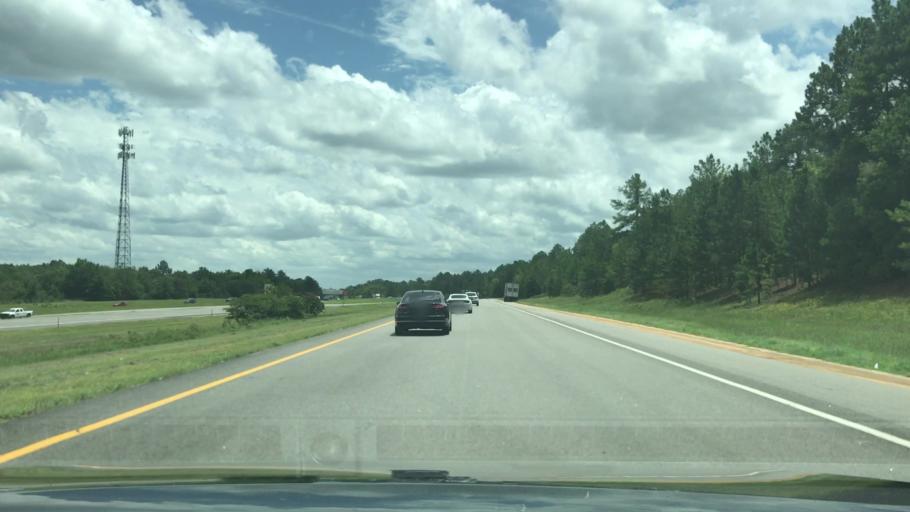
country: US
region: South Carolina
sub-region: Lexington County
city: Pineridge
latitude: 33.9245
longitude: -81.0696
